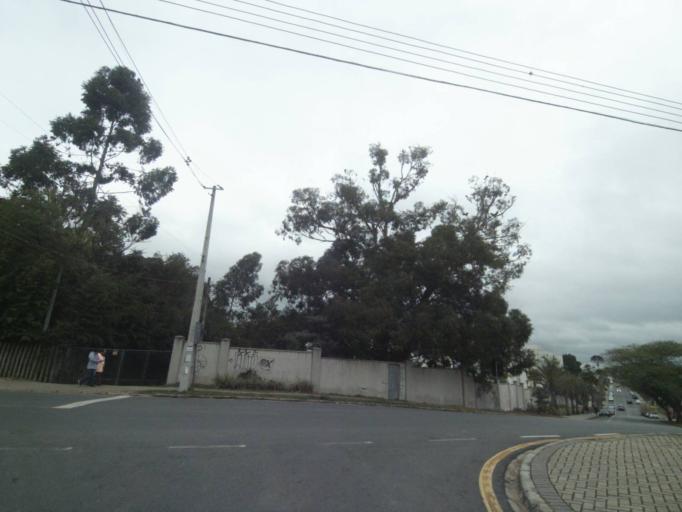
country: BR
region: Parana
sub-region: Curitiba
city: Curitiba
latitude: -25.5088
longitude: -49.2900
